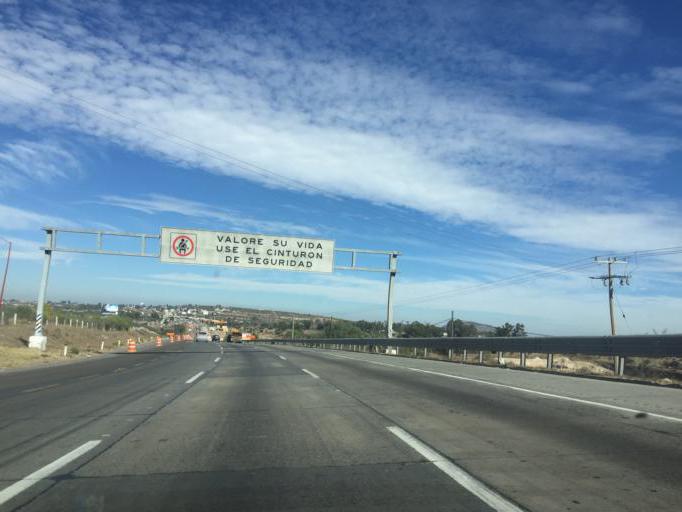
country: MX
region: Queretaro
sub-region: San Juan del Rio
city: Paso de Mata
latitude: 20.3169
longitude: -99.9310
